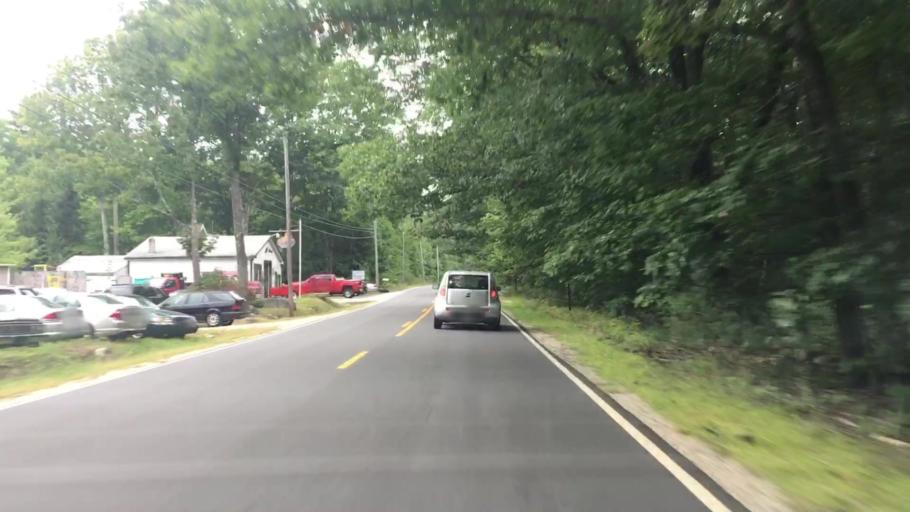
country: US
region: Maine
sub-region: Cumberland County
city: New Gloucester
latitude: 43.8857
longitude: -70.2512
